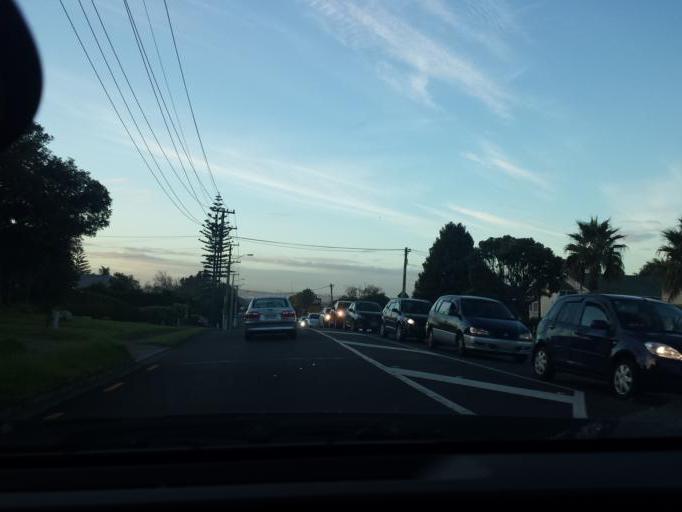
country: NZ
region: Auckland
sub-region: Auckland
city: Tamaki
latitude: -36.8945
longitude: 174.8397
